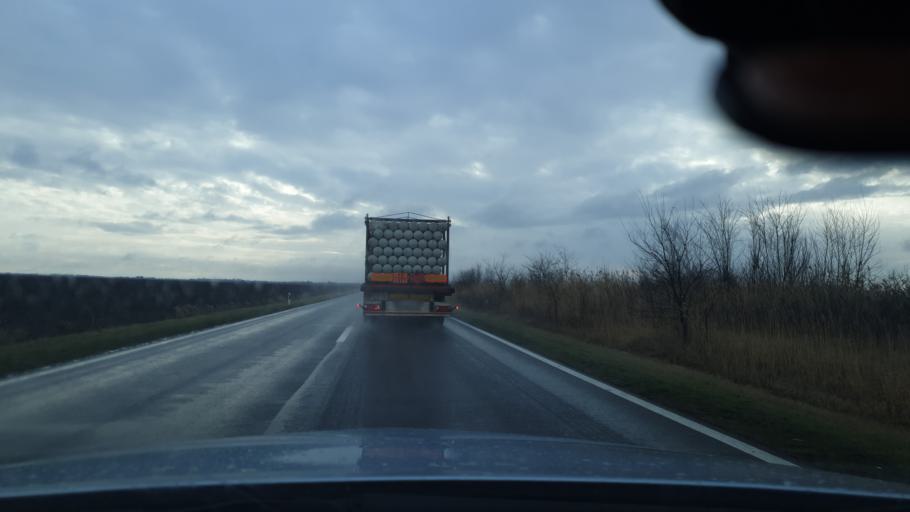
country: RS
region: Autonomna Pokrajina Vojvodina
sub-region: Juznobanatski Okrug
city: Kovin
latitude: 44.7885
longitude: 20.9197
